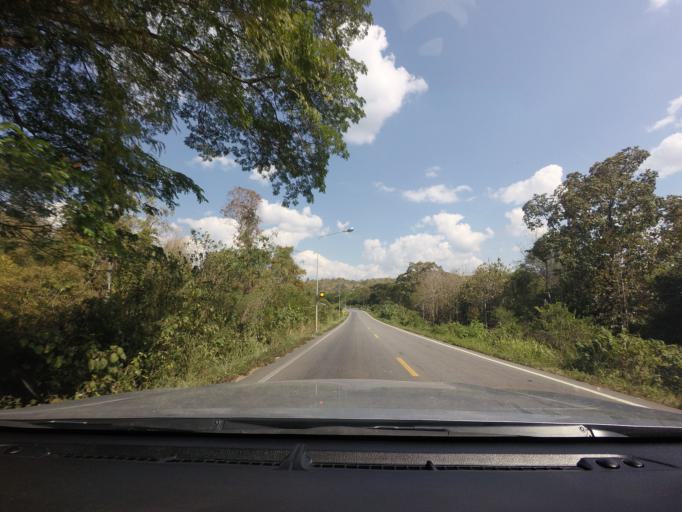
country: TH
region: Chiang Mai
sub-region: Amphoe Chiang Dao
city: Chiang Dao
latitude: 19.4536
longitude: 98.9914
